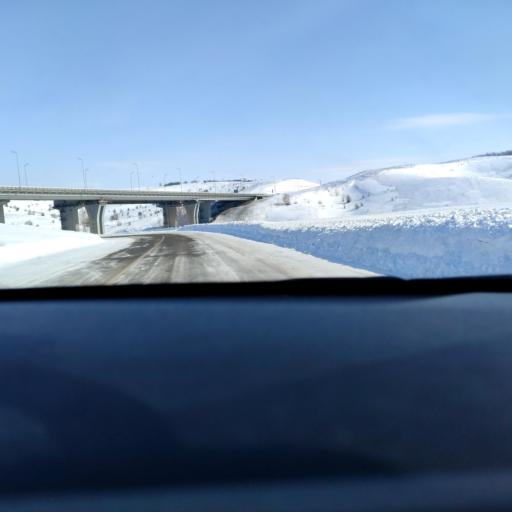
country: RU
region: Tatarstan
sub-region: Alekseyevskiy Rayon
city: Alekseyevskoye
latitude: 55.3787
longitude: 49.9630
